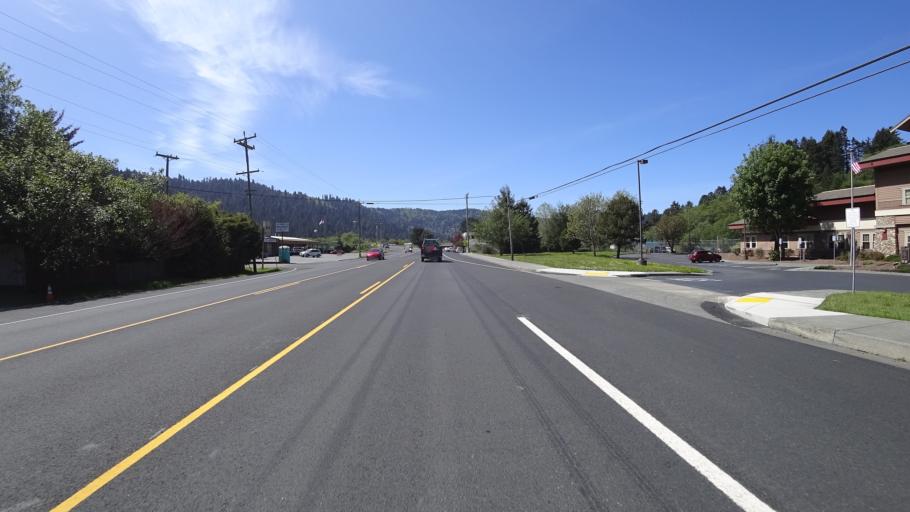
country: US
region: California
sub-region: Humboldt County
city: Westhaven-Moonstone
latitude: 41.2913
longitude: -124.0577
